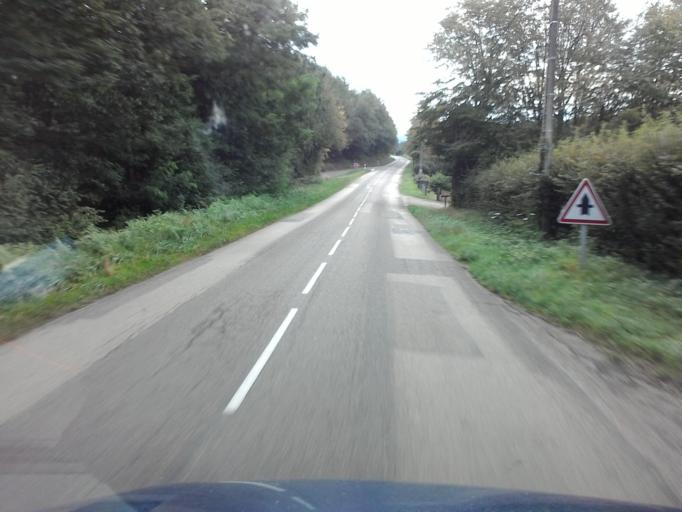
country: FR
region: Bourgogne
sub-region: Departement de la Nievre
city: Chateau-Chinon(Ville)
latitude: 47.0866
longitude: 3.9234
